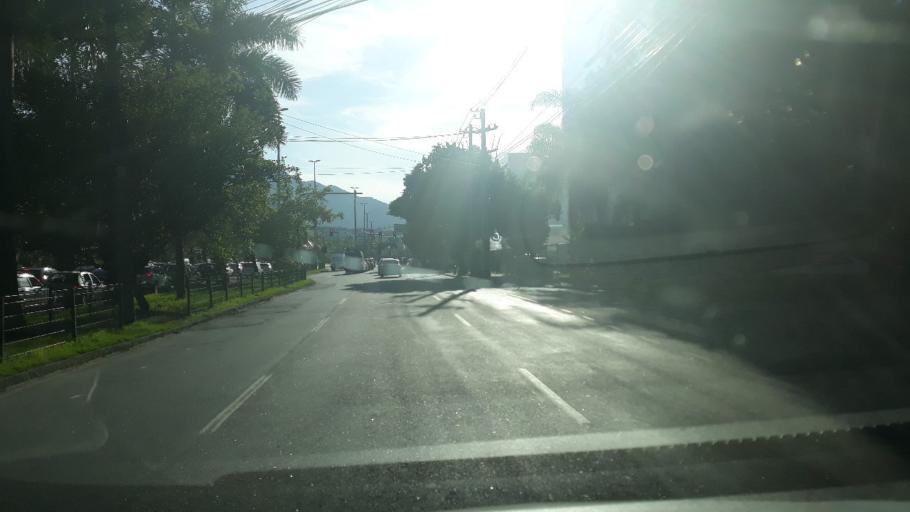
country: BR
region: Rio de Janeiro
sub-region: Sao Joao De Meriti
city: Sao Joao de Meriti
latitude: -22.9736
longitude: -43.3676
